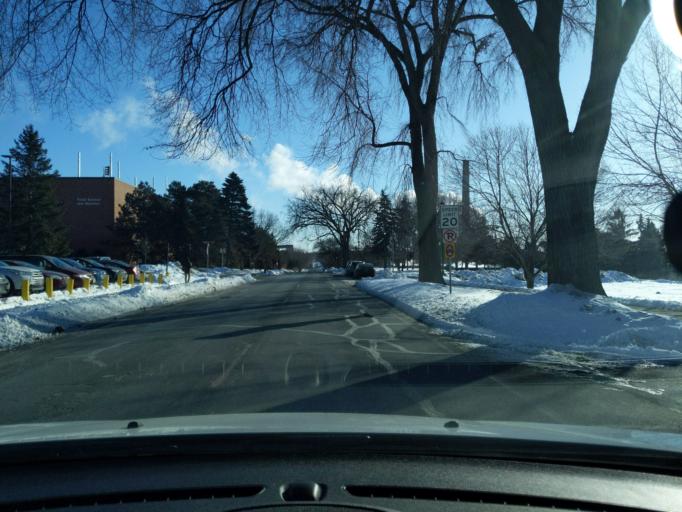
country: US
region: Minnesota
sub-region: Ramsey County
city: Falcon Heights
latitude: 44.9808
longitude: -93.1863
